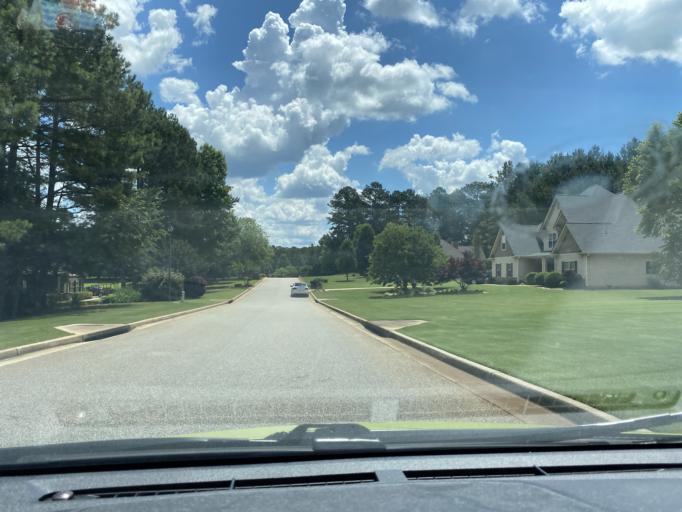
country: US
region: Georgia
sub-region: Fayette County
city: Peachtree City
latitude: 33.4298
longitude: -84.6741
